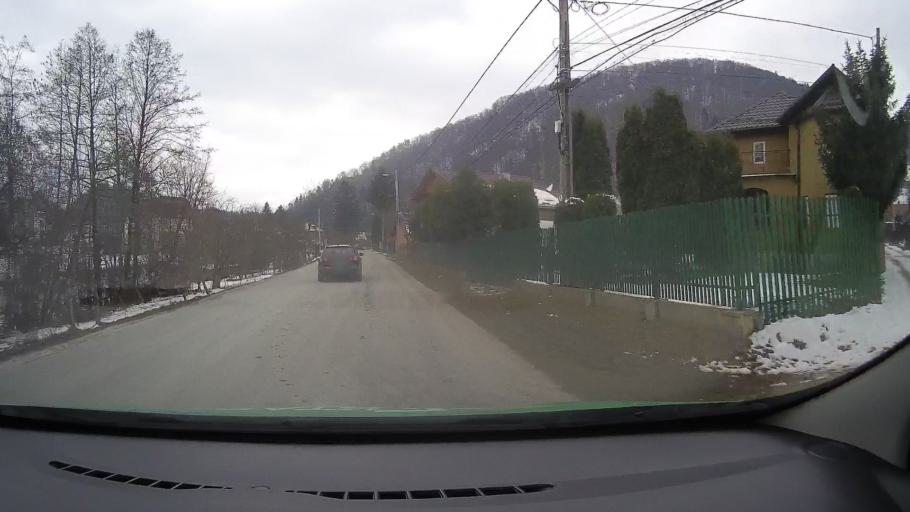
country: RO
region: Brasov
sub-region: Comuna Bran
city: Bran
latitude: 45.5218
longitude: 25.3663
